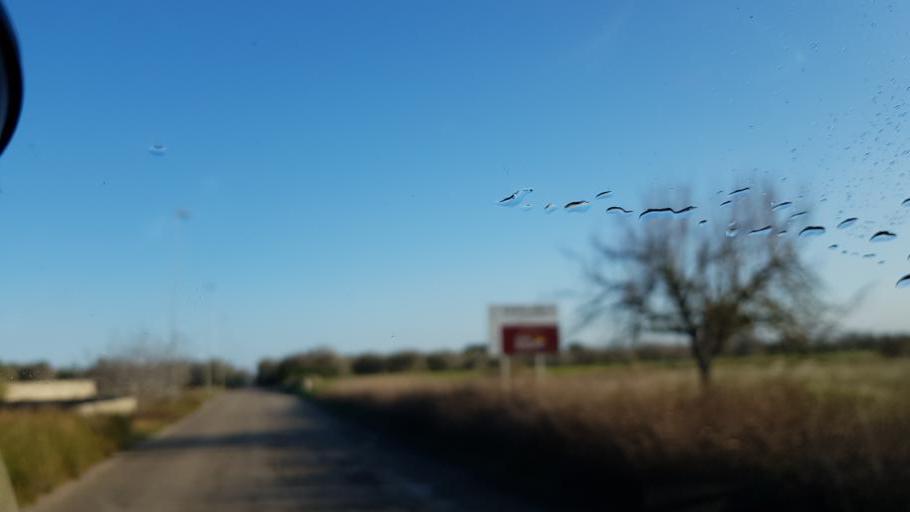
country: IT
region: Apulia
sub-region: Provincia di Brindisi
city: Torchiarolo
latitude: 40.5054
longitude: 18.1011
